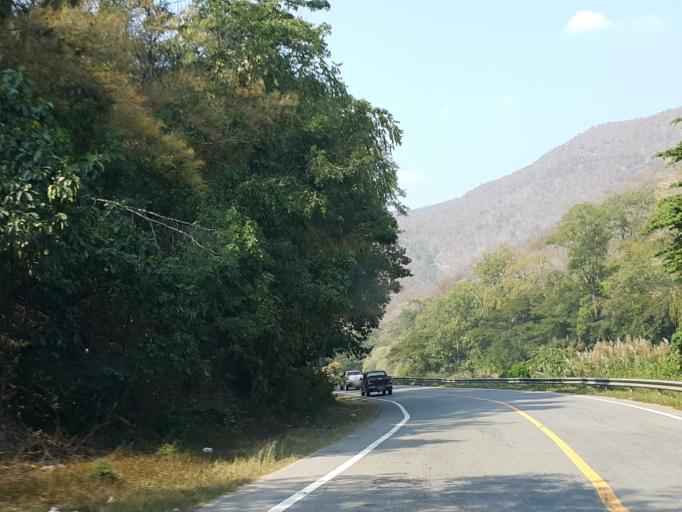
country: TH
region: Chiang Mai
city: Hot
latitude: 18.2338
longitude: 98.5416
